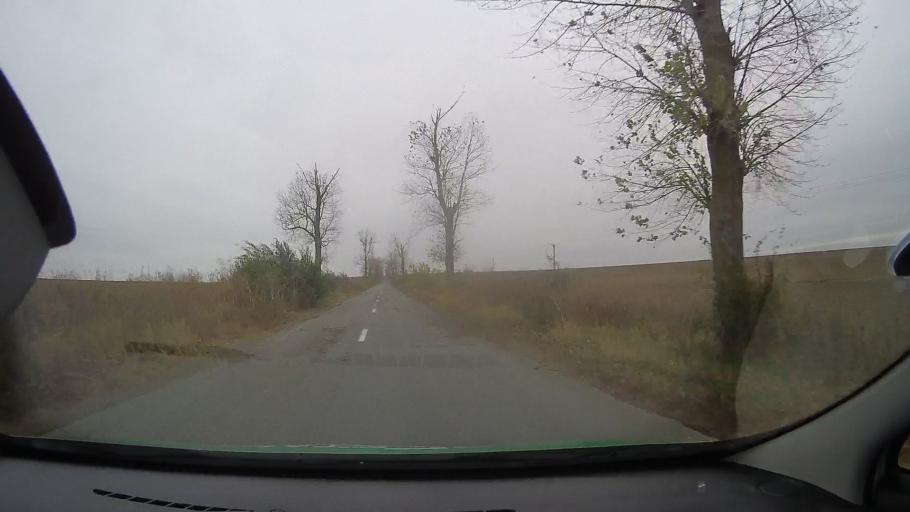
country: RO
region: Constanta
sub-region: Comuna Pantelimon
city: Pantelimon
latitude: 44.5558
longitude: 28.3250
